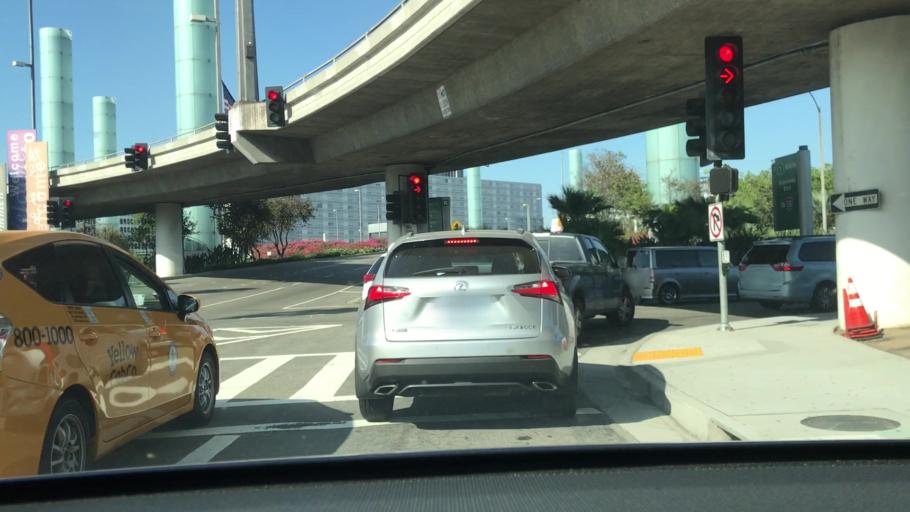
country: US
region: California
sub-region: Los Angeles County
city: El Segundo
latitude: 33.9438
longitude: -118.3976
